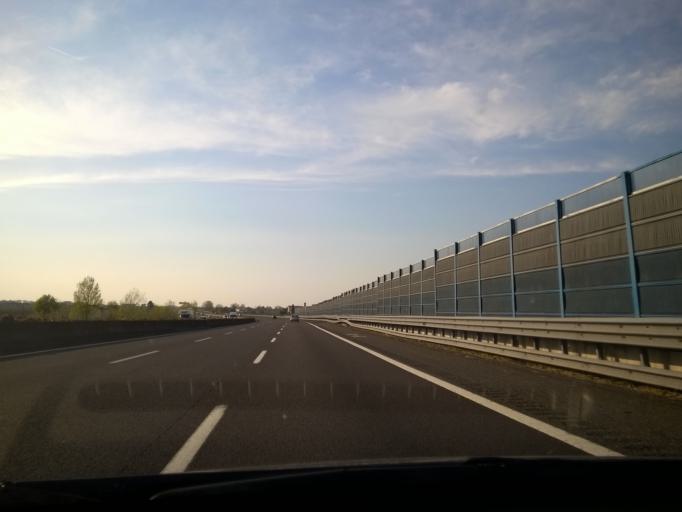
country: IT
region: Emilia-Romagna
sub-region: Provincia di Ravenna
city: Granarolo
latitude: 44.3165
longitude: 11.9230
